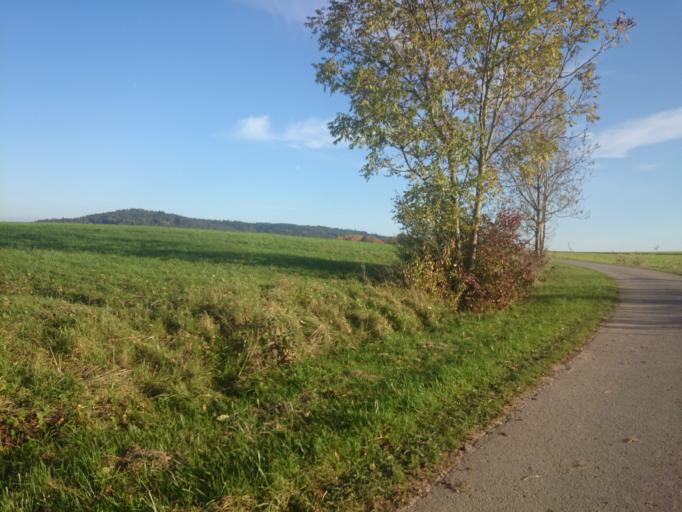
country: DE
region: Bavaria
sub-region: Regierungsbezirk Mittelfranken
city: Thalmassing
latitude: 49.1357
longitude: 11.2573
